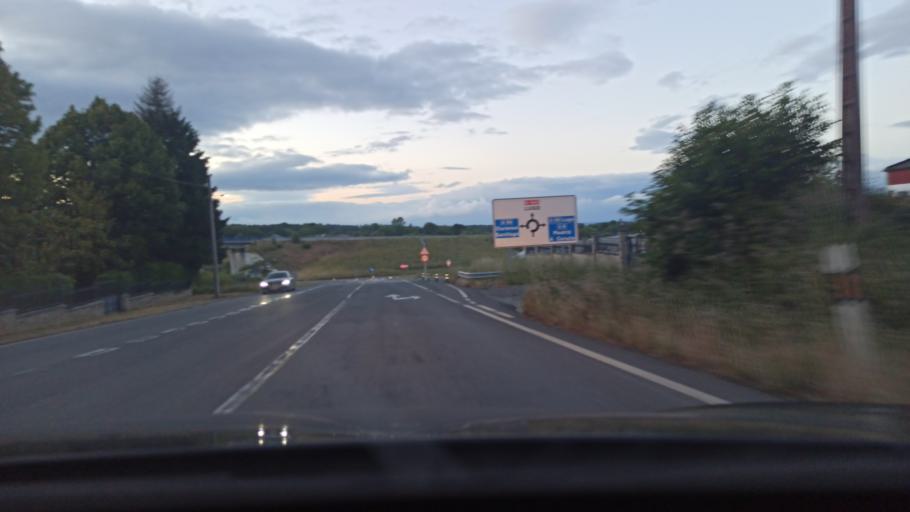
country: ES
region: Galicia
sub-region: Provincia de Lugo
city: Ourol
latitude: 42.9365
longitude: -7.6312
